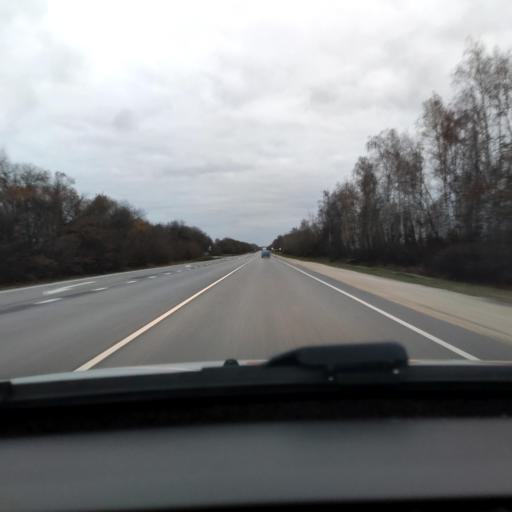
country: RU
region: Lipetsk
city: Borinskoye
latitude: 52.4021
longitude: 39.2390
